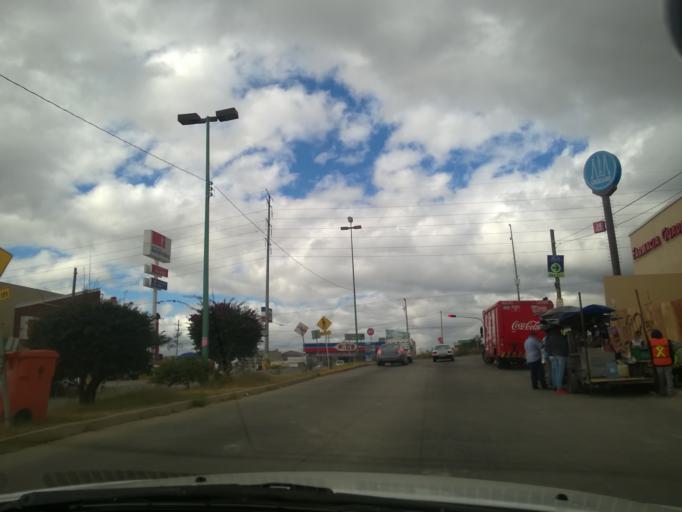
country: MX
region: Guanajuato
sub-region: Leon
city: La Ermita
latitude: 21.1526
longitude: -101.7293
